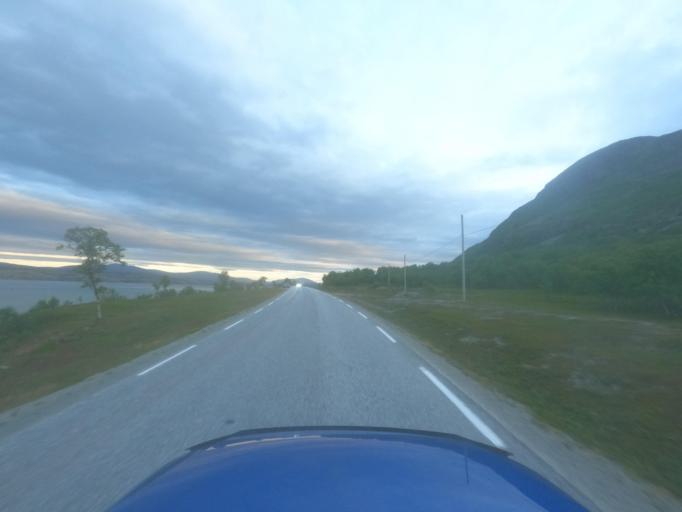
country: NO
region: Finnmark Fylke
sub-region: Porsanger
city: Lakselv
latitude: 70.1372
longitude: 24.9133
